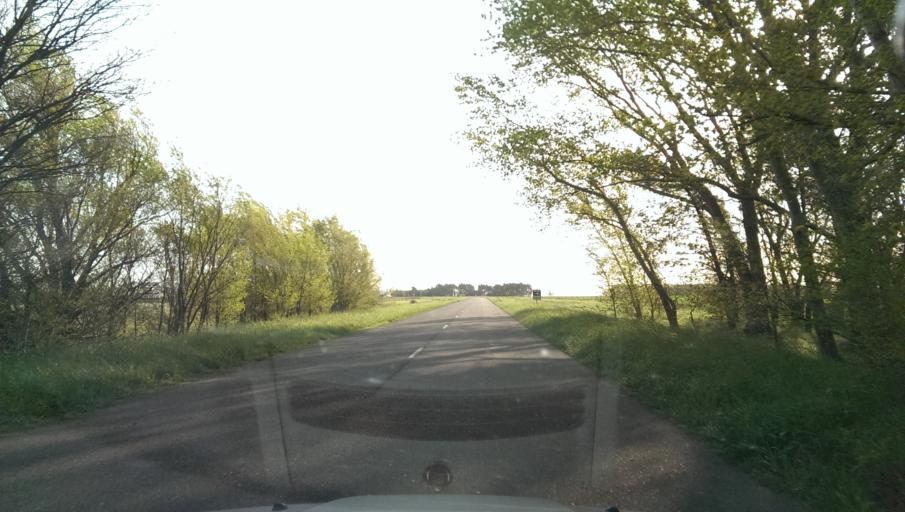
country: AR
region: Buenos Aires
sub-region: Partido de Coronel Suarez
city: Coronel Suarez
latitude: -37.7717
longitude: -61.7041
